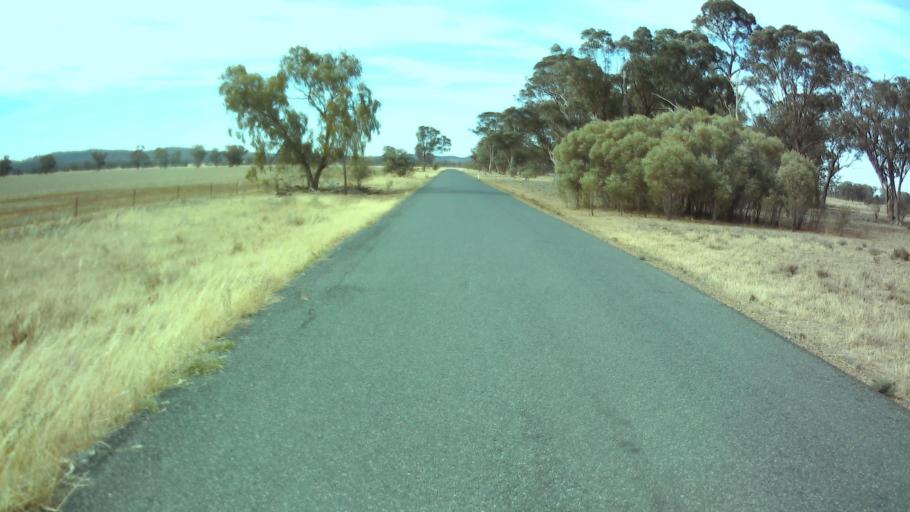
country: AU
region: New South Wales
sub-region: Weddin
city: Grenfell
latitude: -33.8614
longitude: 147.8598
